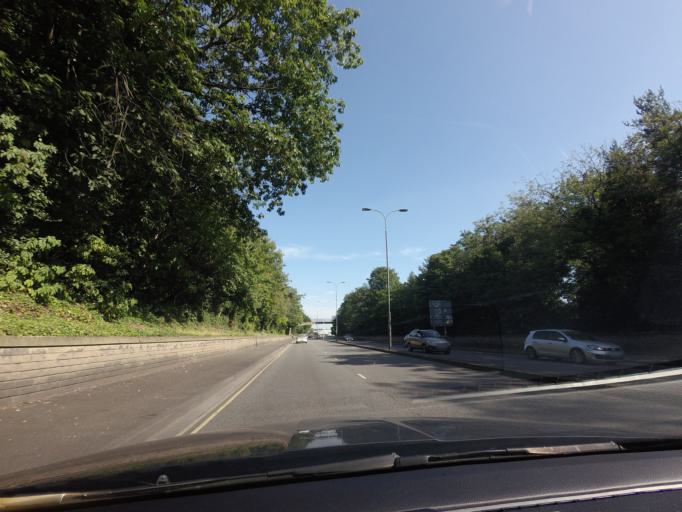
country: GB
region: England
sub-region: Derbyshire
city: Chesterfield
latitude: 53.2347
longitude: -1.4347
